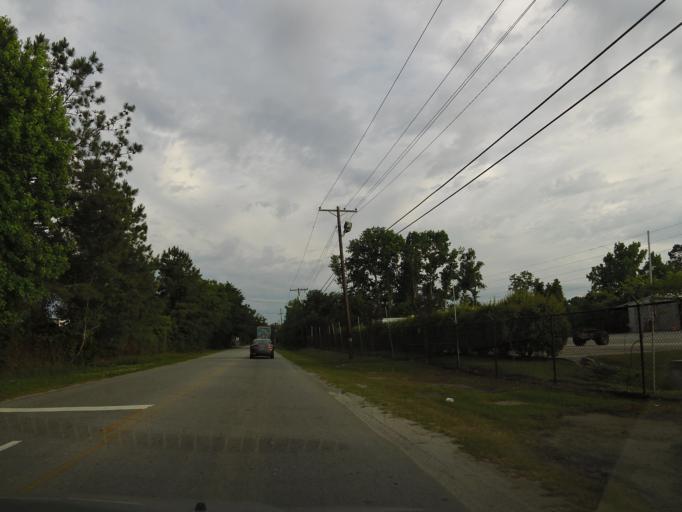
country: US
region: Georgia
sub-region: Chatham County
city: Garden City
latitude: 32.0892
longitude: -81.1992
